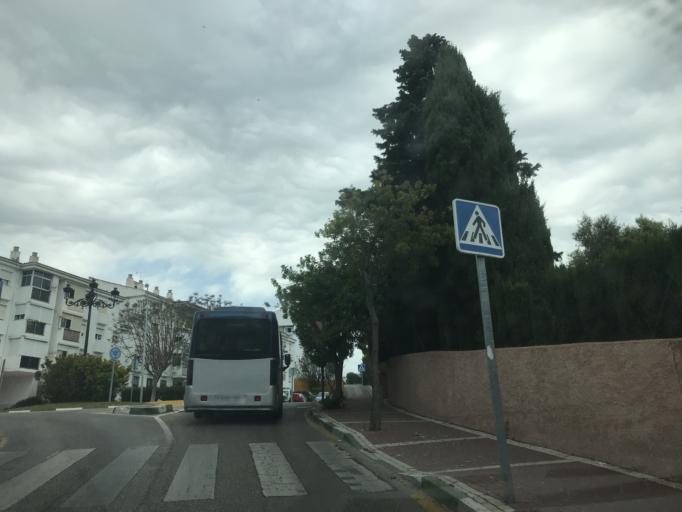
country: ES
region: Andalusia
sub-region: Provincia de Malaga
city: Estepona
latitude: 36.4297
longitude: -5.1371
